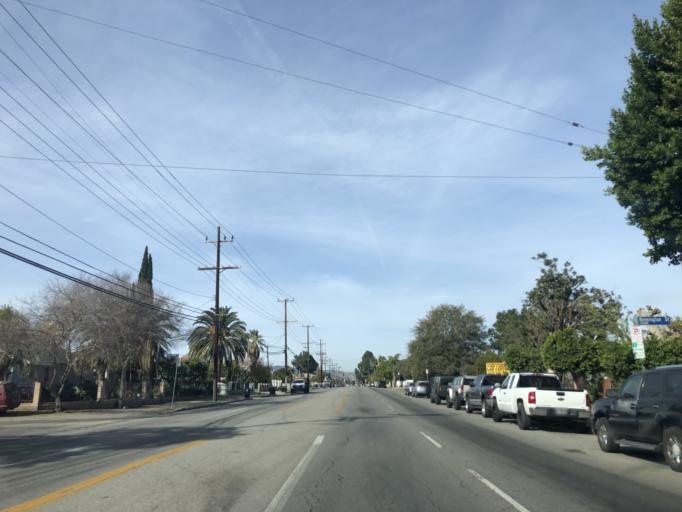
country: US
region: California
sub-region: Los Angeles County
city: San Fernando
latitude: 34.2533
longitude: -118.4263
